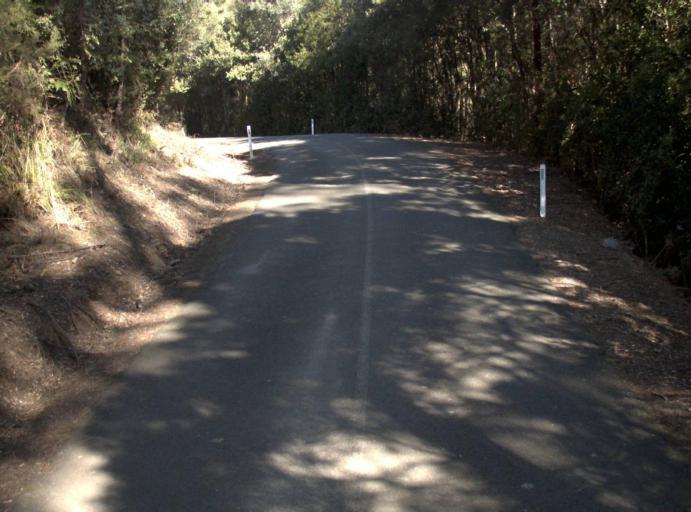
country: AU
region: Tasmania
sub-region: Launceston
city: Mayfield
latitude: -41.2994
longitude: 147.1999
